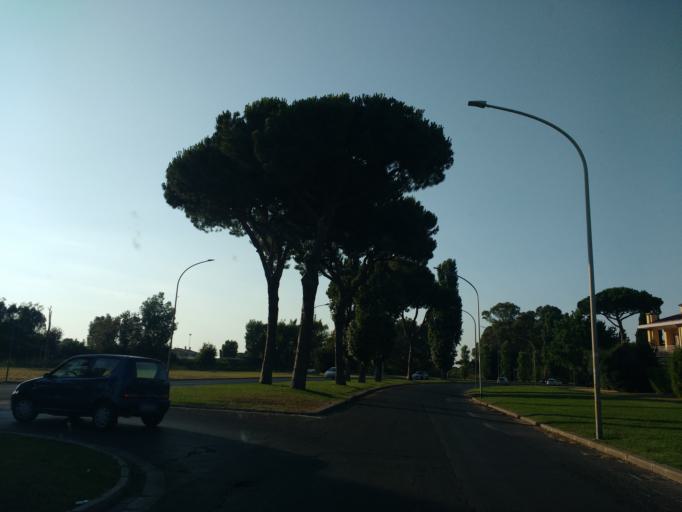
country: IT
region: Latium
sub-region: Citta metropolitana di Roma Capitale
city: Acilia-Castel Fusano-Ostia Antica
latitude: 41.7521
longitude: 12.3506
